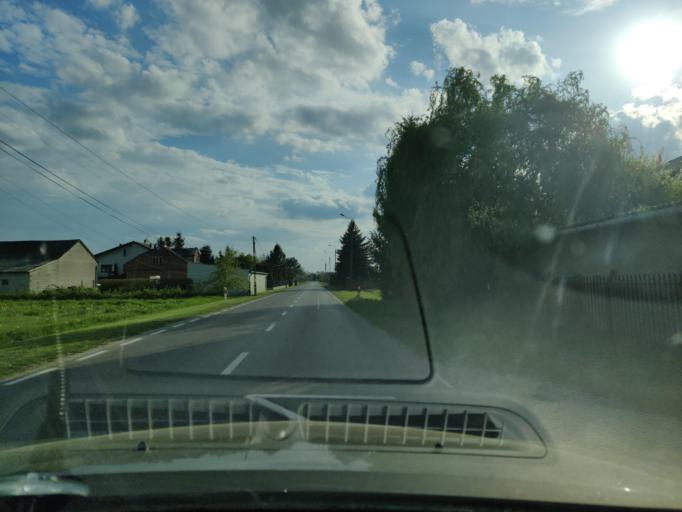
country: PL
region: Masovian Voivodeship
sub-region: Powiat otwocki
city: Jozefow
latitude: 52.1086
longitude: 21.1836
